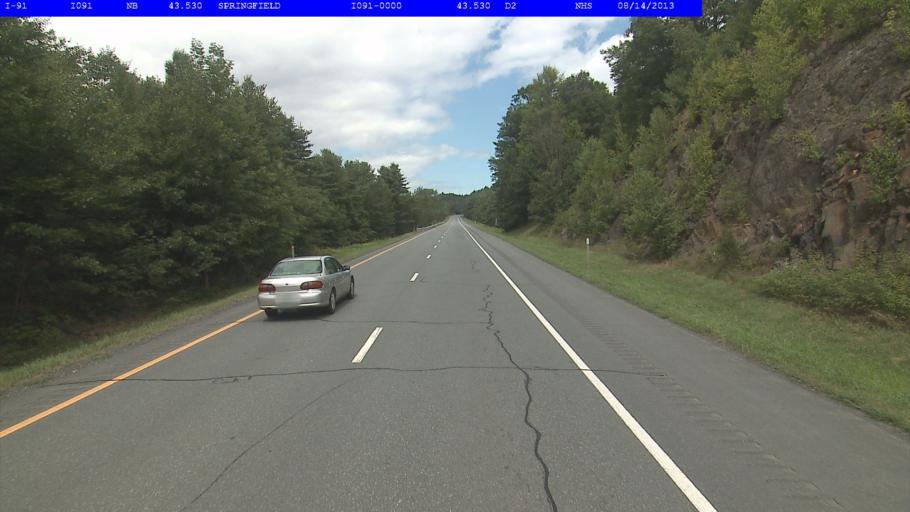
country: US
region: New Hampshire
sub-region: Sullivan County
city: Charlestown
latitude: 43.2919
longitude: -72.4270
